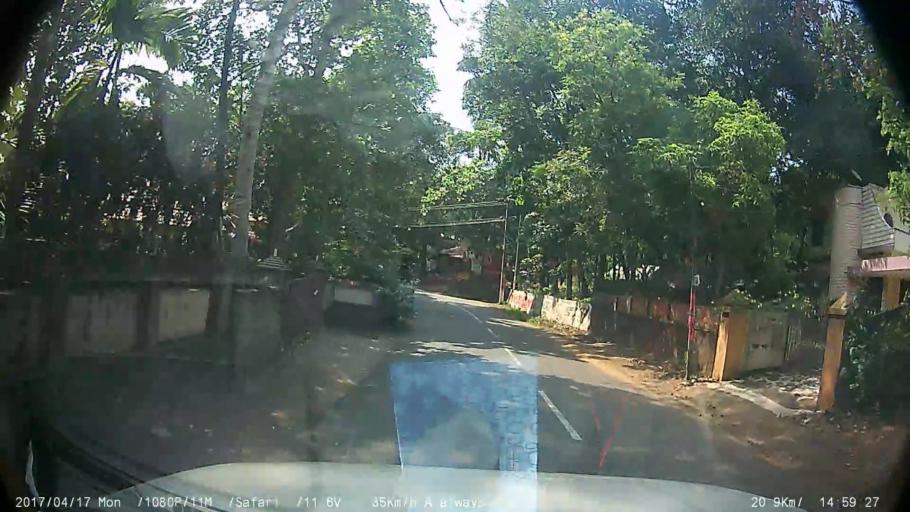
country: IN
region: Kerala
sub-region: Ernakulam
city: Piravam
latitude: 9.8396
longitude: 76.4931
